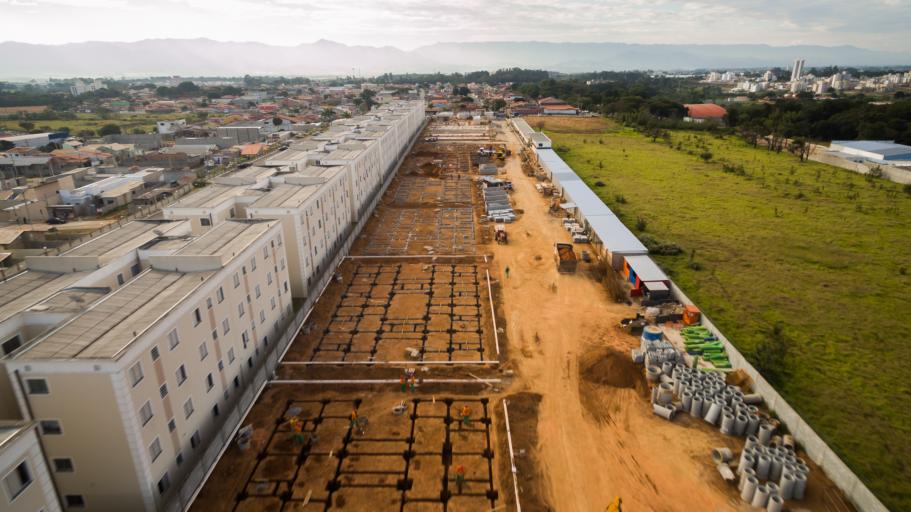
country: BR
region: Sao Paulo
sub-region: Taubate
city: Taubate
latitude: -23.0399
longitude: -45.6008
